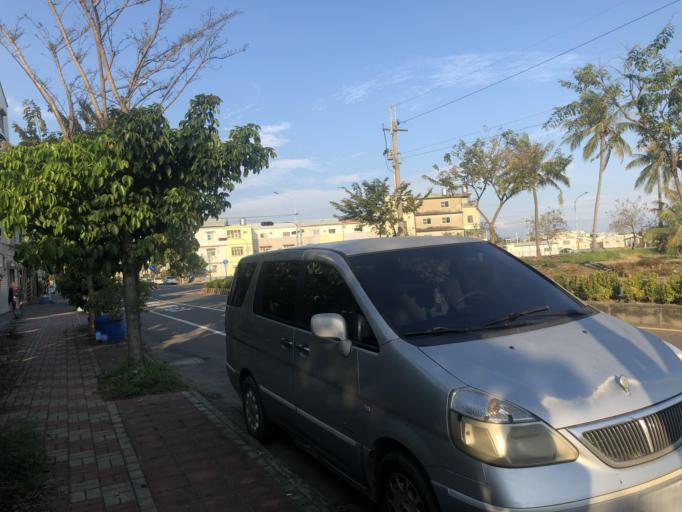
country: TW
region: Taiwan
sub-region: Tainan
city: Tainan
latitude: 23.0367
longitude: 120.1850
